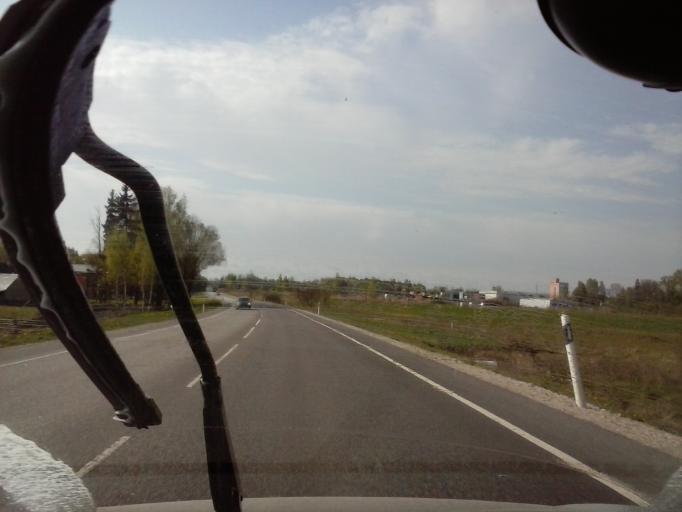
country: EE
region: Tartu
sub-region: UElenurme vald
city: Ulenurme
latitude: 58.3075
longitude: 26.7178
